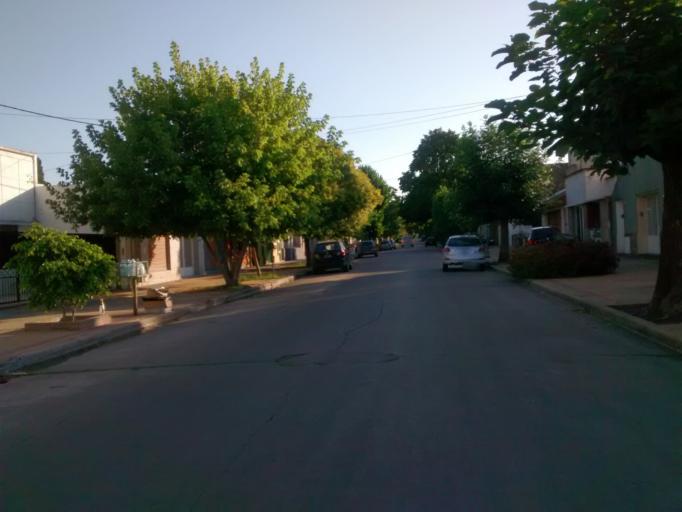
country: AR
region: Buenos Aires
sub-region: Partido de La Plata
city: La Plata
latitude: -34.9159
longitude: -57.9279
